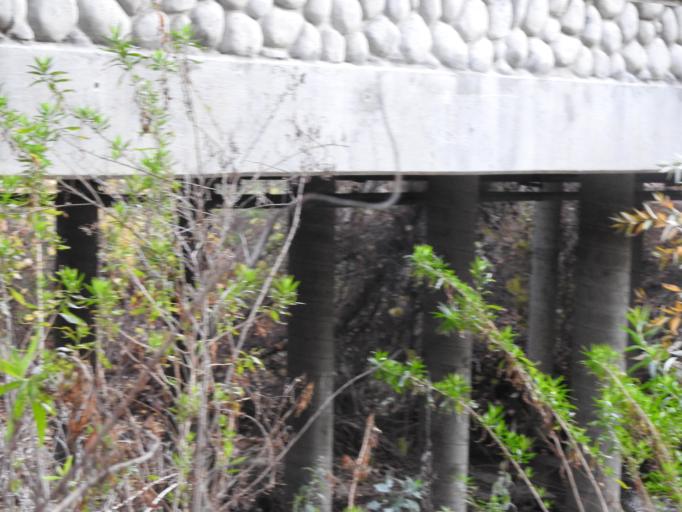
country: US
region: California
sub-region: San Diego County
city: Valley Center
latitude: 33.2574
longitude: -117.0692
